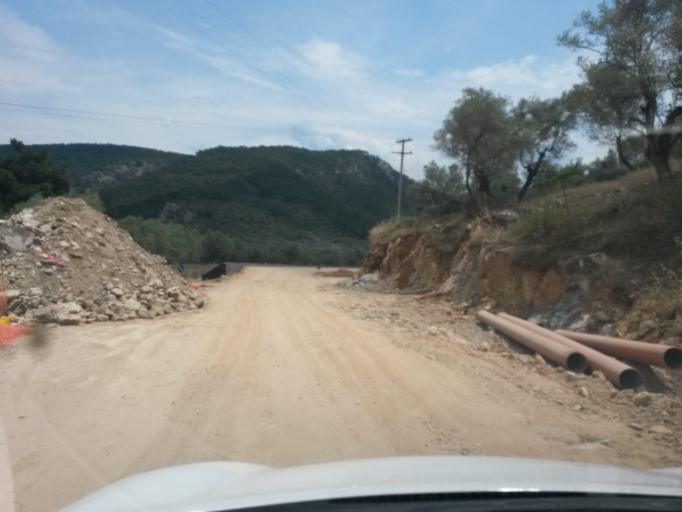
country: GR
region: North Aegean
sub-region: Nomos Lesvou
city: Pamfylla
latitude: 39.1779
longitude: 26.4221
